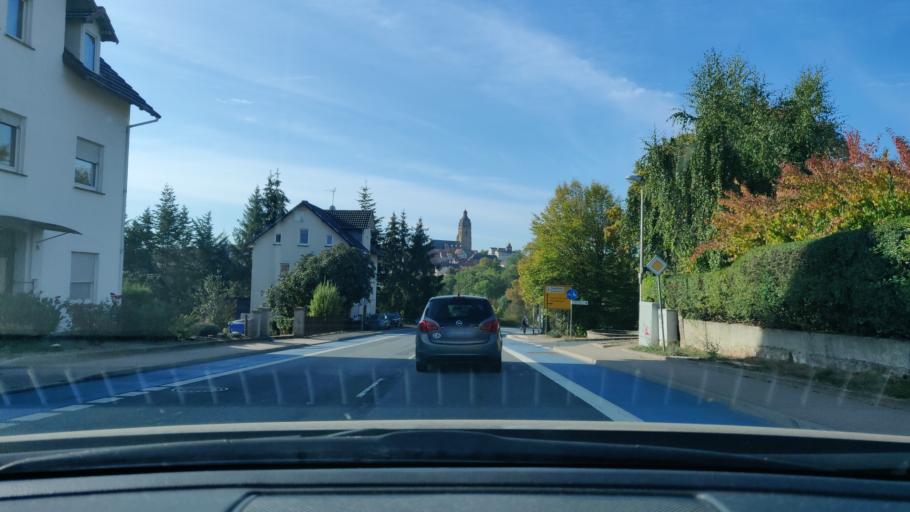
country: DE
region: Hesse
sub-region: Regierungsbezirk Kassel
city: Bad Wildungen
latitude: 51.1254
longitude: 9.1245
